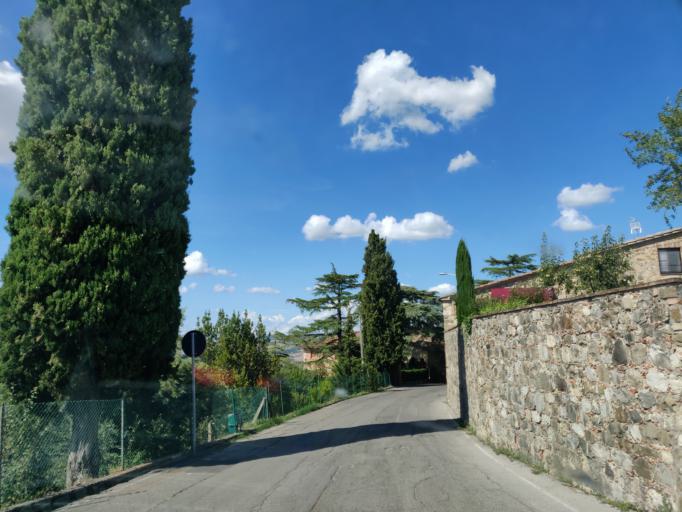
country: IT
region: Tuscany
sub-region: Provincia di Siena
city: Radicofani
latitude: 42.9756
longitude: 11.7401
